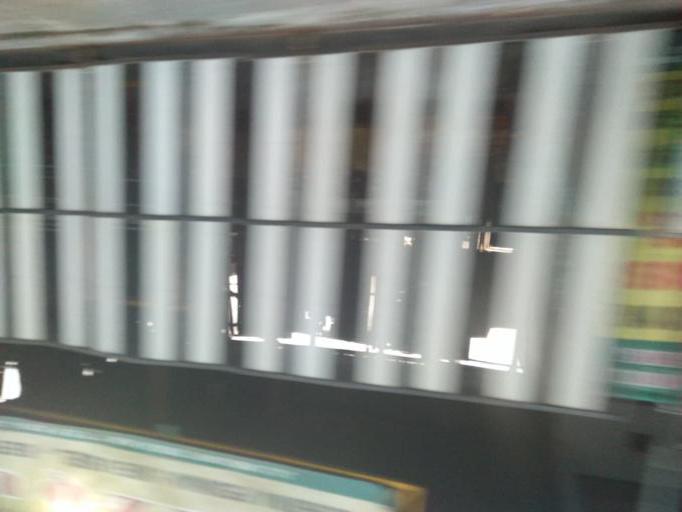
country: ID
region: Daerah Istimewa Yogyakarta
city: Sewon
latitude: -7.8397
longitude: 110.3917
